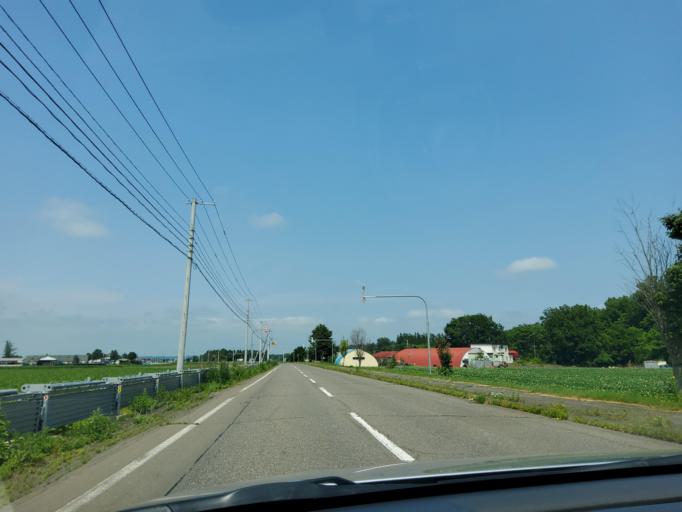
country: JP
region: Hokkaido
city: Obihiro
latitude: 42.8711
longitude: 143.0236
